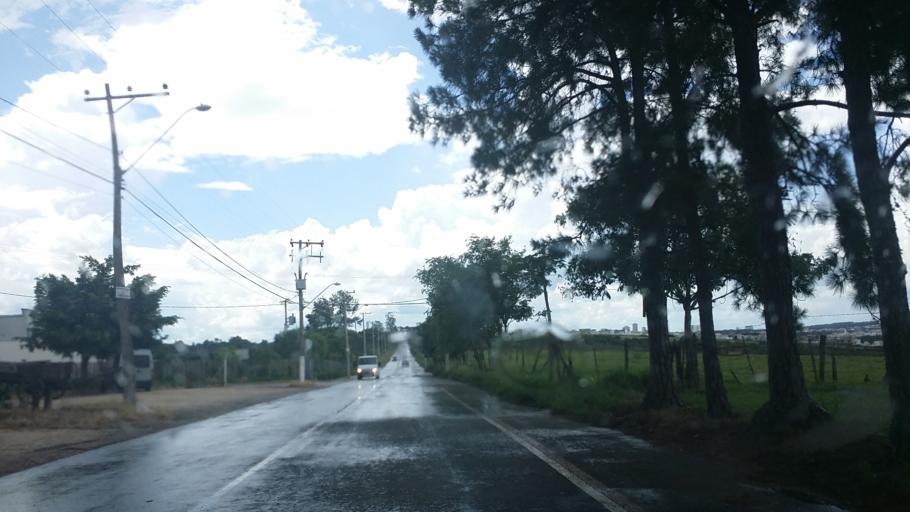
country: BR
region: Sao Paulo
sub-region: Indaiatuba
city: Indaiatuba
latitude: -23.1341
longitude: -47.1695
